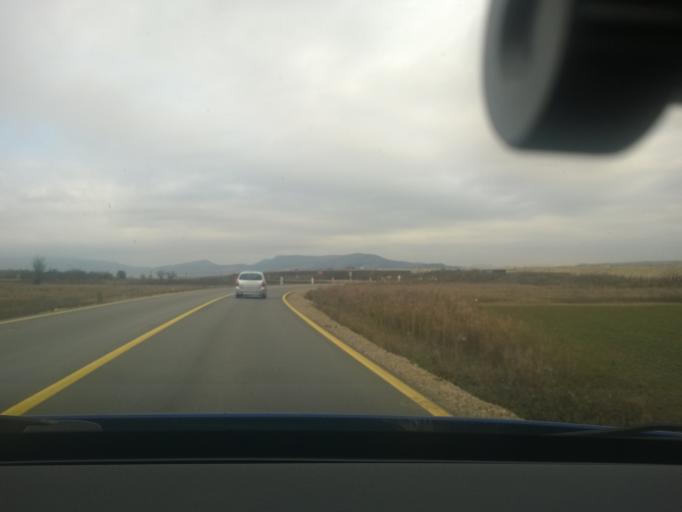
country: RS
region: Central Serbia
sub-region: Pirotski Okrug
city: Pirot
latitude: 43.1174
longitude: 22.6237
